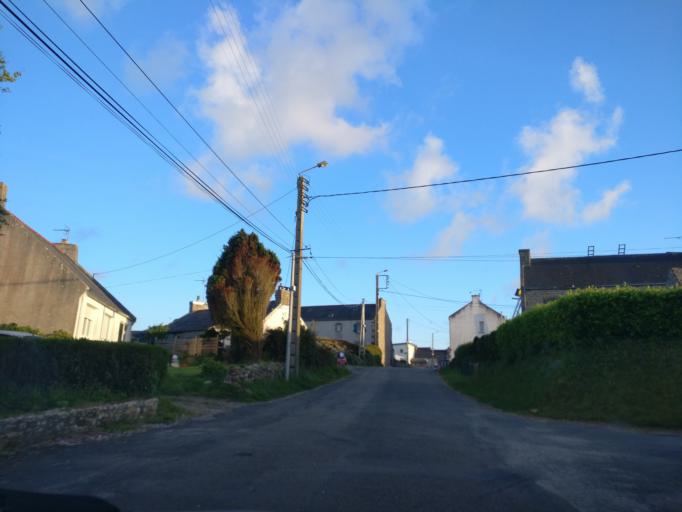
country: FR
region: Brittany
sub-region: Departement du Finistere
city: Lampaul-Plouarzel
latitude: 48.4490
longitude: -4.7600
